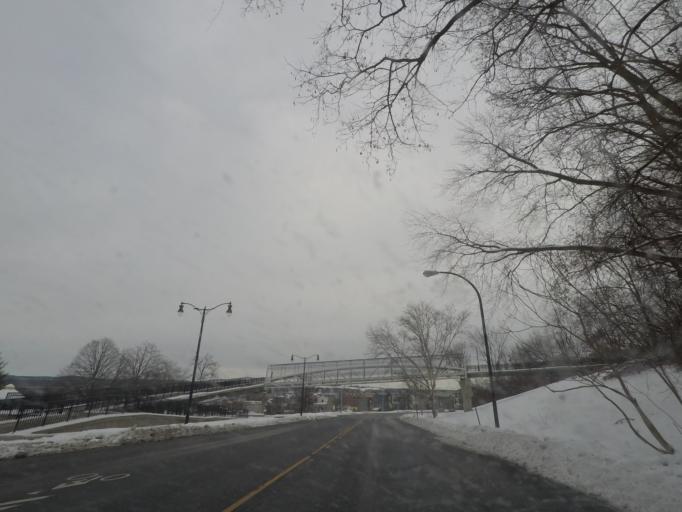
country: US
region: New York
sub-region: Albany County
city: Albany
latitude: 42.6621
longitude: -73.7517
